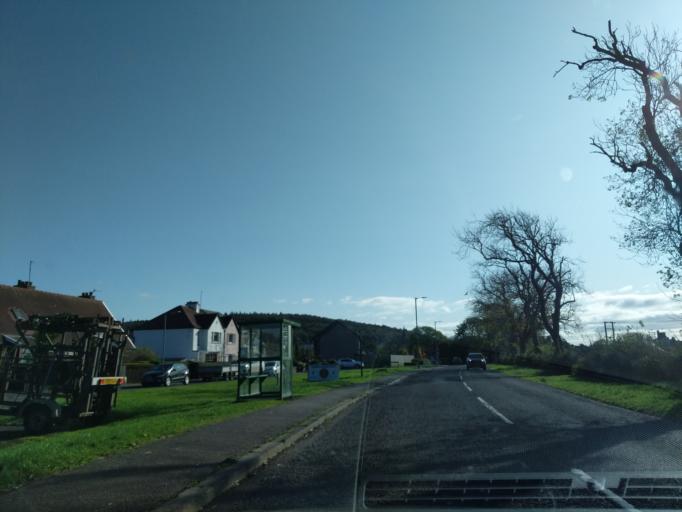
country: GB
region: Scotland
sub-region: Dumfries and Galloway
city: Kirkcudbright
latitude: 54.8416
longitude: -4.0539
